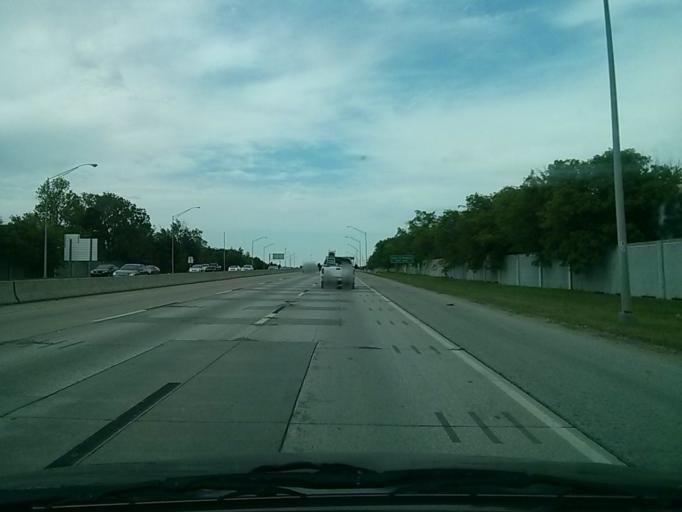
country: US
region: Oklahoma
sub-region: Tulsa County
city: Broken Arrow
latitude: 36.1263
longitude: -95.8596
